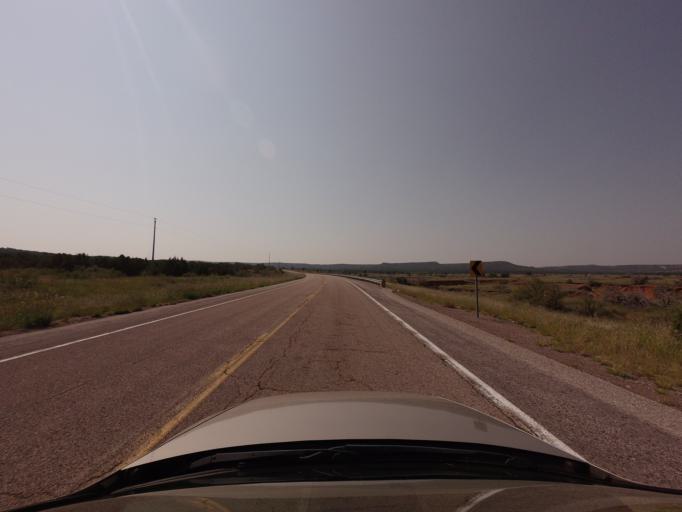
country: US
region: New Mexico
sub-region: Quay County
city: Tucumcari
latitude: 34.8427
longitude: -103.7605
